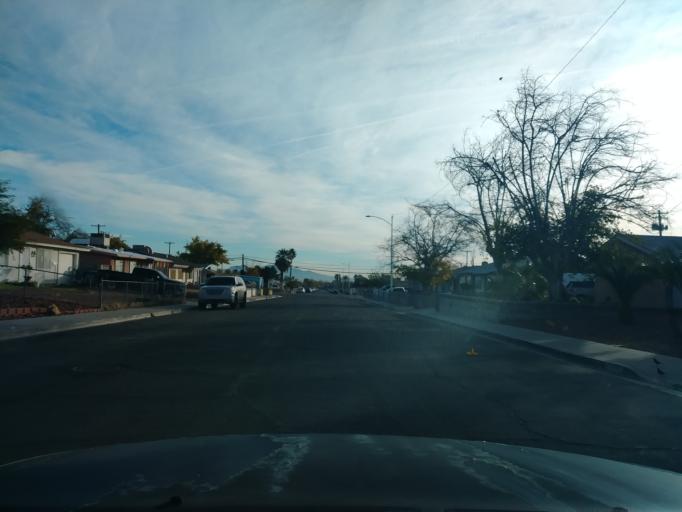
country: US
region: Nevada
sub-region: Clark County
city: Spring Valley
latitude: 36.1615
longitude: -115.2344
